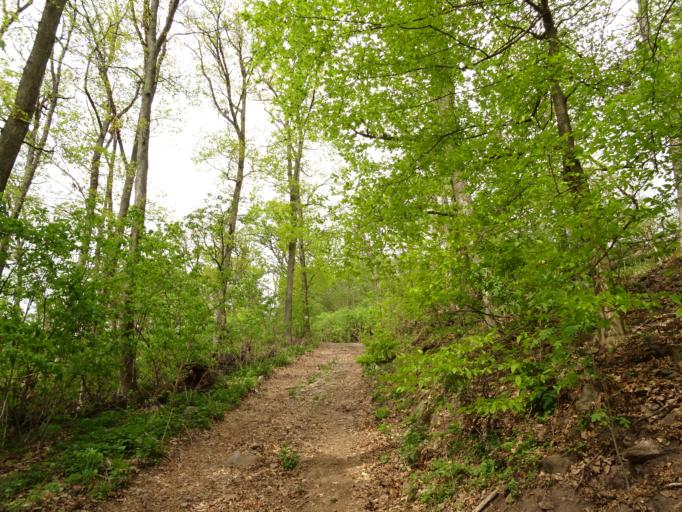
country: HU
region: Borsod-Abauj-Zemplen
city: Satoraljaujhely
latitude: 48.4020
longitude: 21.6333
